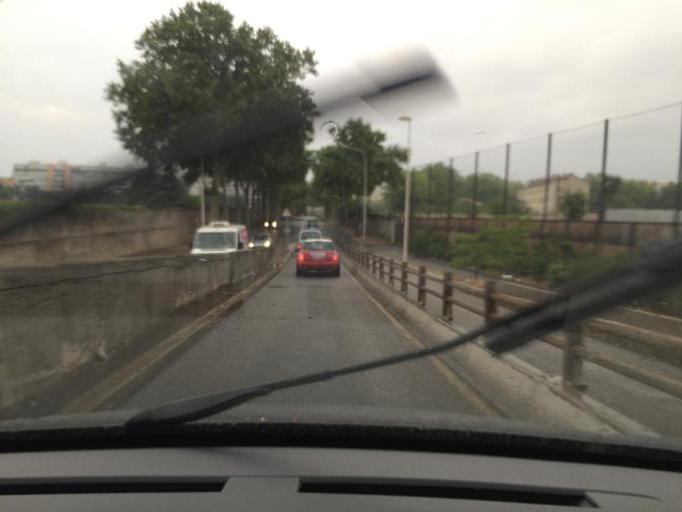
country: FR
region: Rhone-Alpes
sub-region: Departement du Rhone
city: Lyon
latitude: 45.7427
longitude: 4.8570
